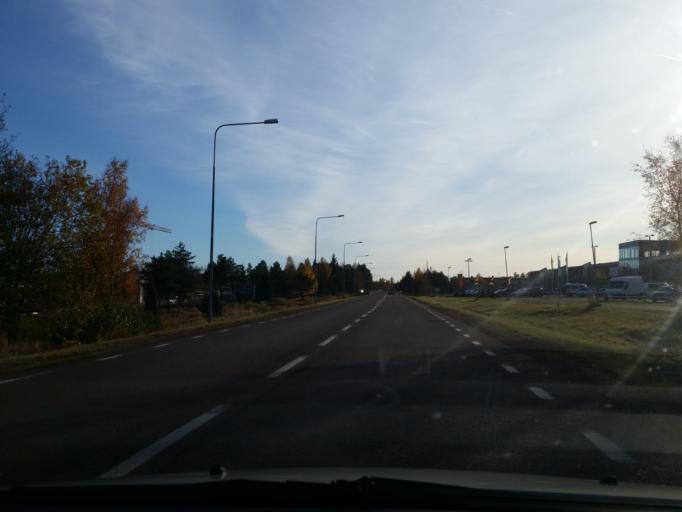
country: AX
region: Alands landsbygd
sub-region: Jomala
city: Jomala
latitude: 60.1311
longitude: 19.9349
